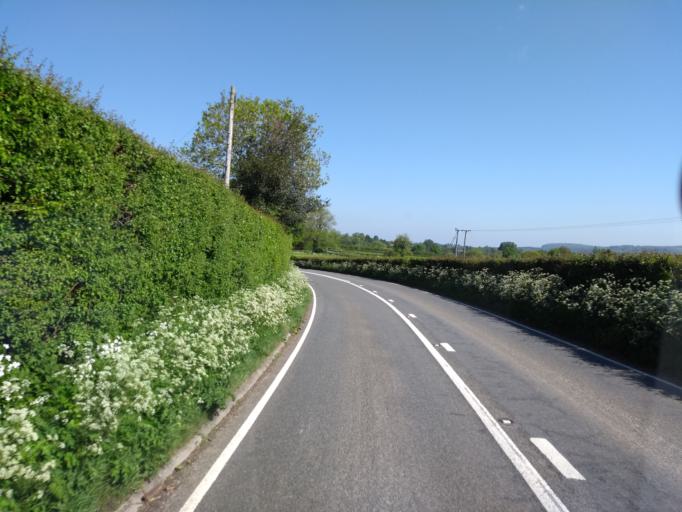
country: GB
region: England
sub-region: Somerset
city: Chard
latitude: 50.8400
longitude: -2.9598
